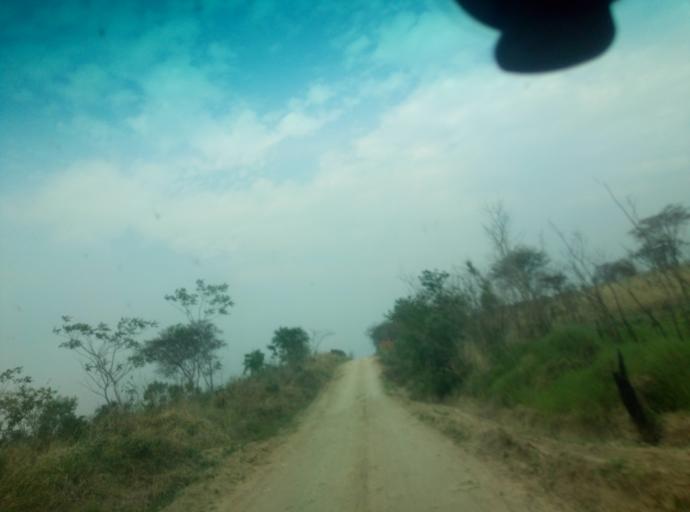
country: PY
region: Caaguazu
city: San Joaquin
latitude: -25.1006
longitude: -56.1338
